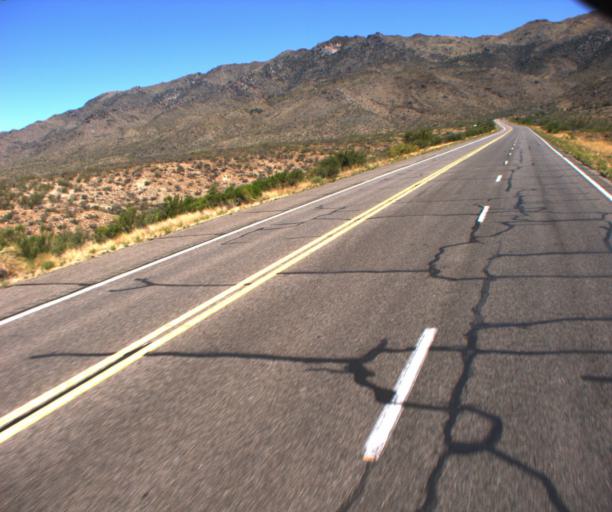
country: US
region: Arizona
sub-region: Yavapai County
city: Congress
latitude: 34.1990
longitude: -112.8092
